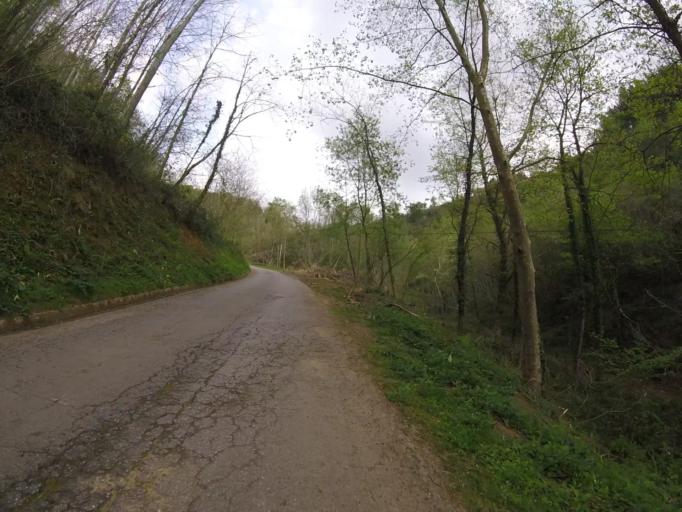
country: ES
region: Basque Country
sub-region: Provincia de Guipuzcoa
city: Anoeta
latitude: 43.1658
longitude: -2.0786
